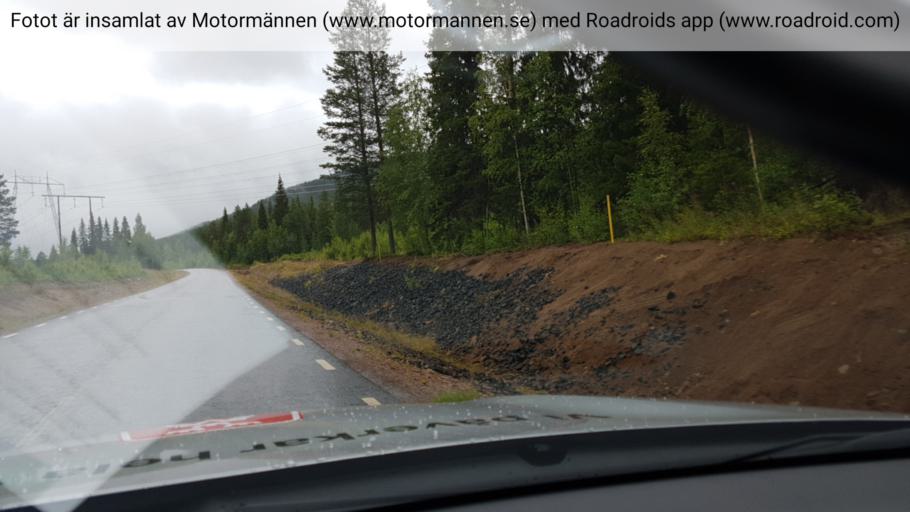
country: SE
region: Norrbotten
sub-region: Gallivare Kommun
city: Gaellivare
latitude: 66.6602
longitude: 20.3742
